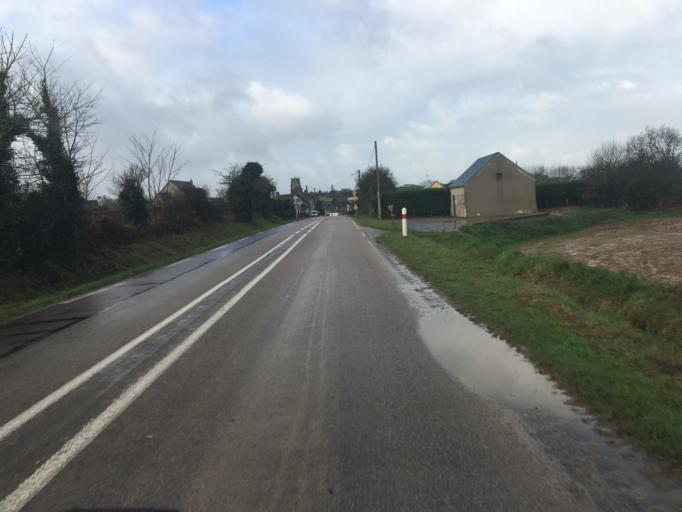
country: FR
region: Lower Normandy
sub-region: Departement de la Manche
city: Saint-Pierre-Eglise
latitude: 49.6706
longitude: -1.3317
